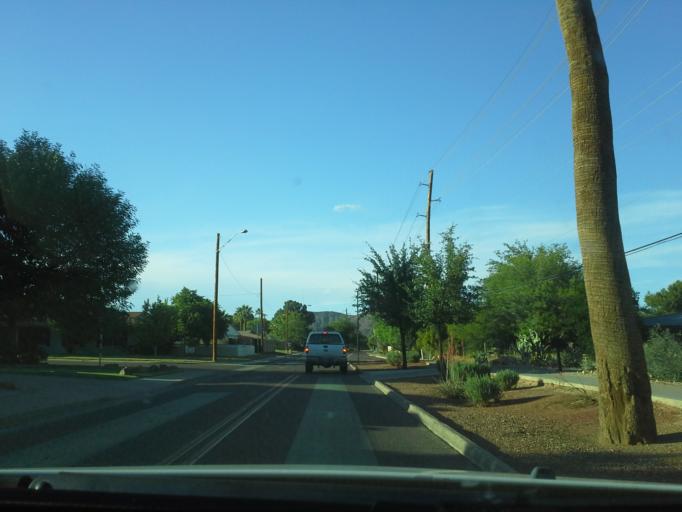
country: US
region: Arizona
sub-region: Maricopa County
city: Glendale
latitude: 33.5607
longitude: -112.0913
